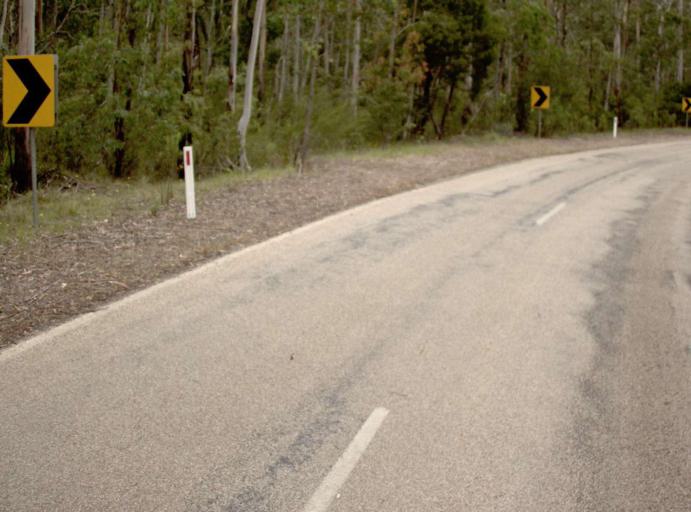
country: AU
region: Victoria
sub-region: East Gippsland
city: Bairnsdale
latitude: -37.6270
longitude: 147.2160
